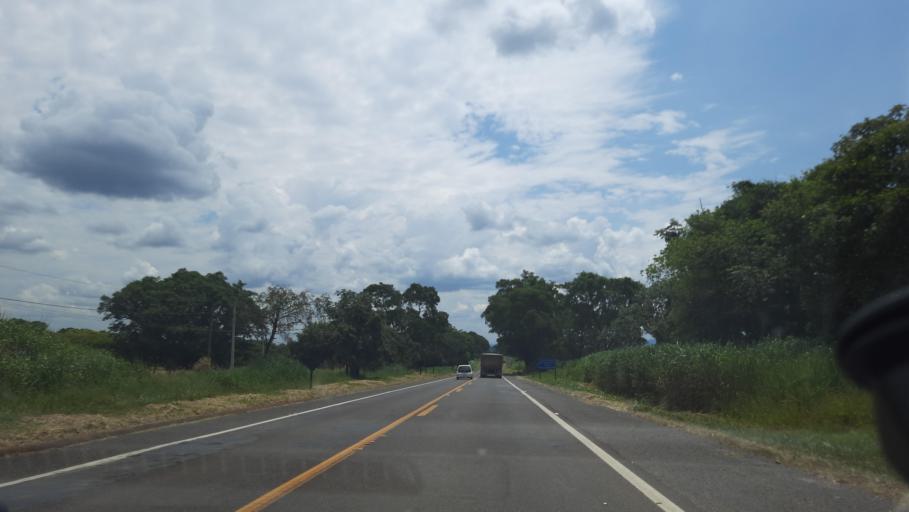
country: BR
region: Sao Paulo
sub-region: Mococa
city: Mococa
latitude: -21.5158
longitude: -47.0341
